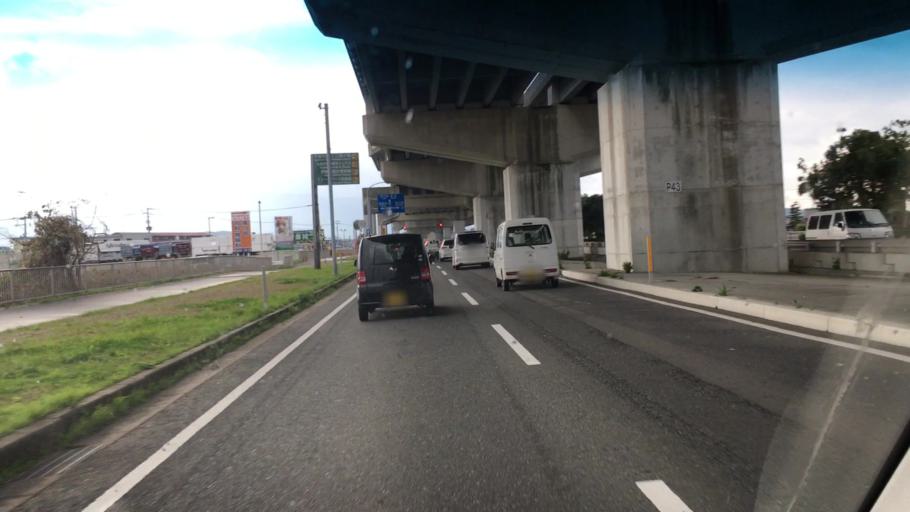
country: JP
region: Fukuoka
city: Maebaru-chuo
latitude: 33.5585
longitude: 130.2300
